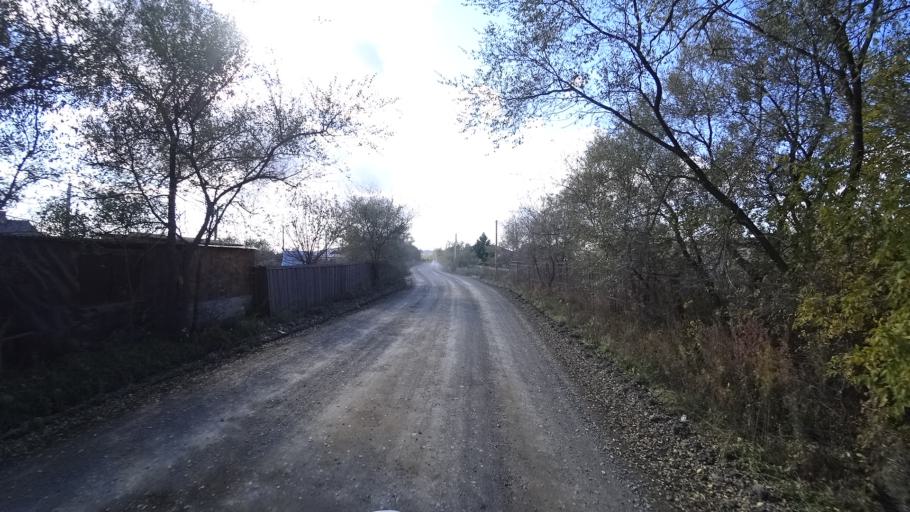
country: RU
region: Khabarovsk Krai
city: Amursk
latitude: 50.0965
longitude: 136.5029
